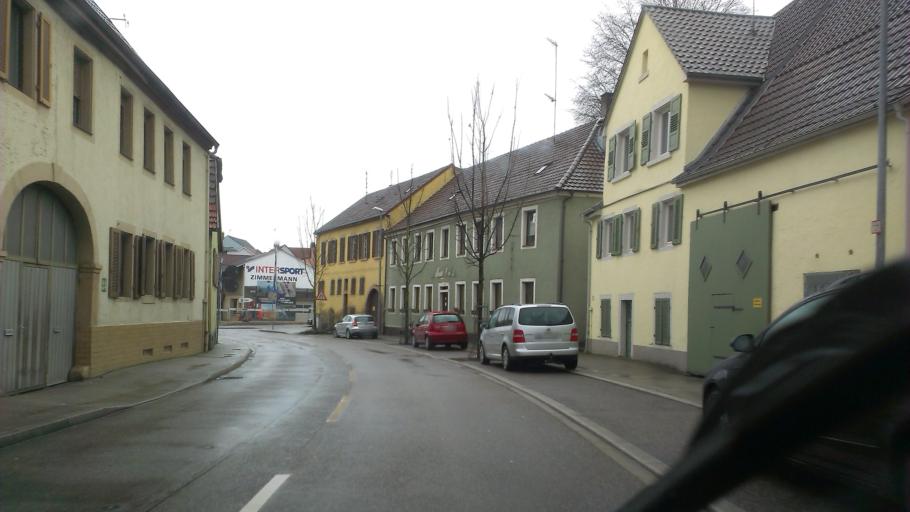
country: DE
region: Baden-Wuerttemberg
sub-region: Karlsruhe Region
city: Gondelsheim
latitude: 49.1030
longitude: 8.6411
